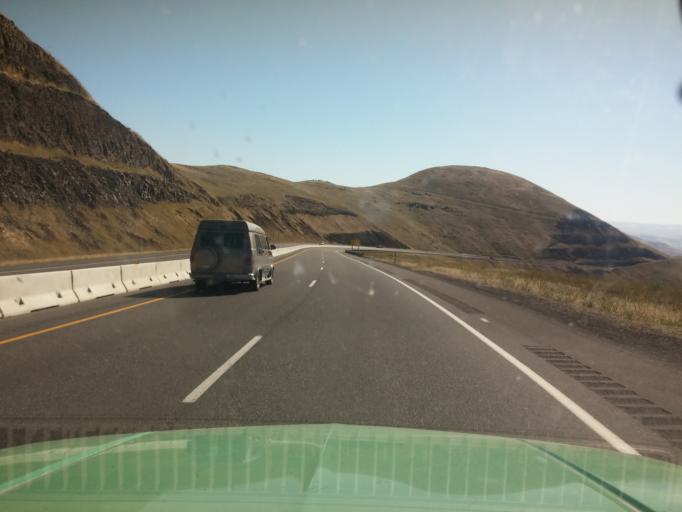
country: US
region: Idaho
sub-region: Nez Perce County
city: Lewiston
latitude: 46.4620
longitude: -116.9898
